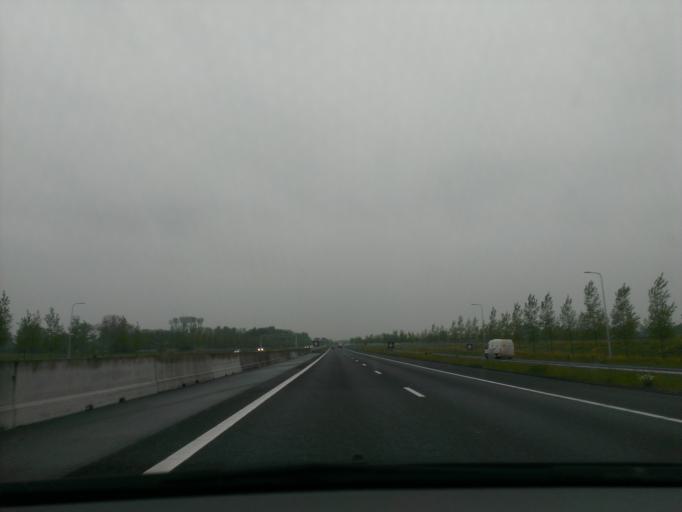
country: NL
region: Gelderland
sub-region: Gemeente Zaltbommel
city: Zaltbommel
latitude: 51.8553
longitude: 5.2215
